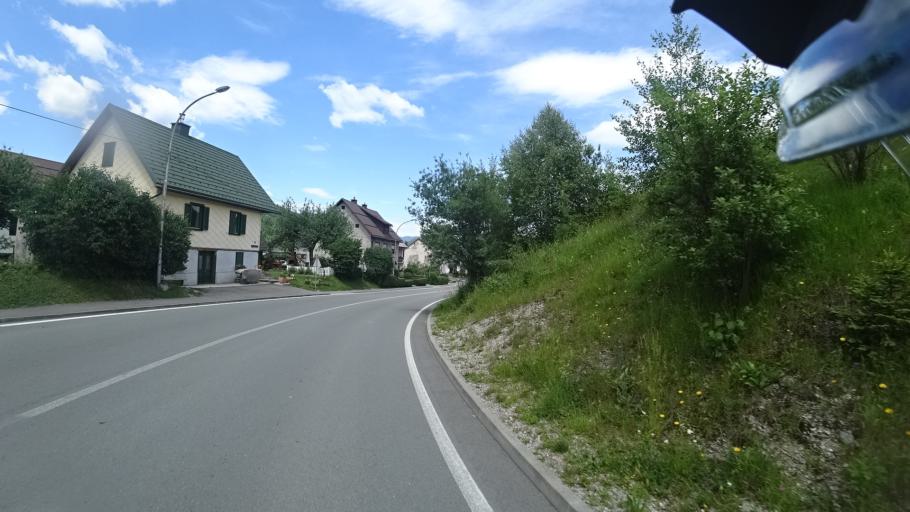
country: SI
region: Osilnica
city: Osilnica
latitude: 45.5122
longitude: 14.6361
